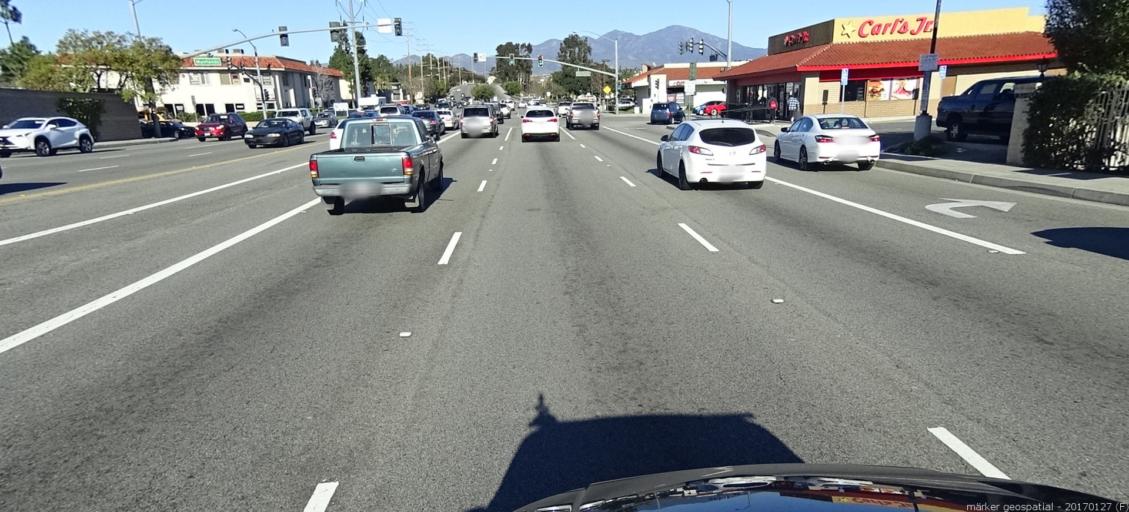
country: US
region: California
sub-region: Orange County
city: Laguna Hills
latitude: 33.6226
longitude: -117.6978
